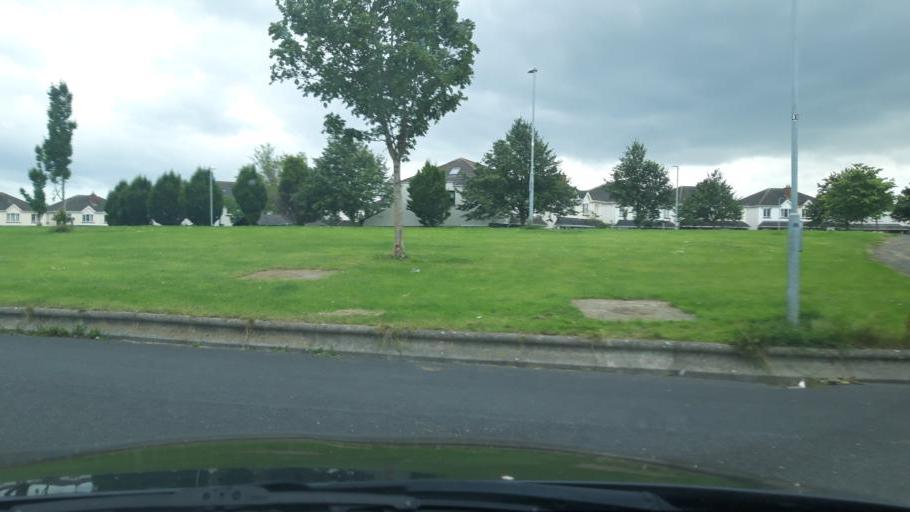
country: IE
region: Leinster
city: Hartstown
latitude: 53.4008
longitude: -6.4219
